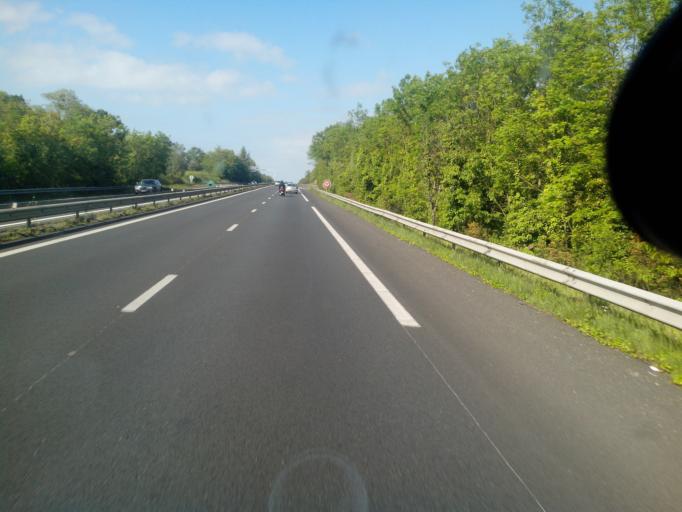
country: FR
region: Lower Normandy
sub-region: Departement du Calvados
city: Troarn
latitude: 49.1800
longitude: -0.2002
